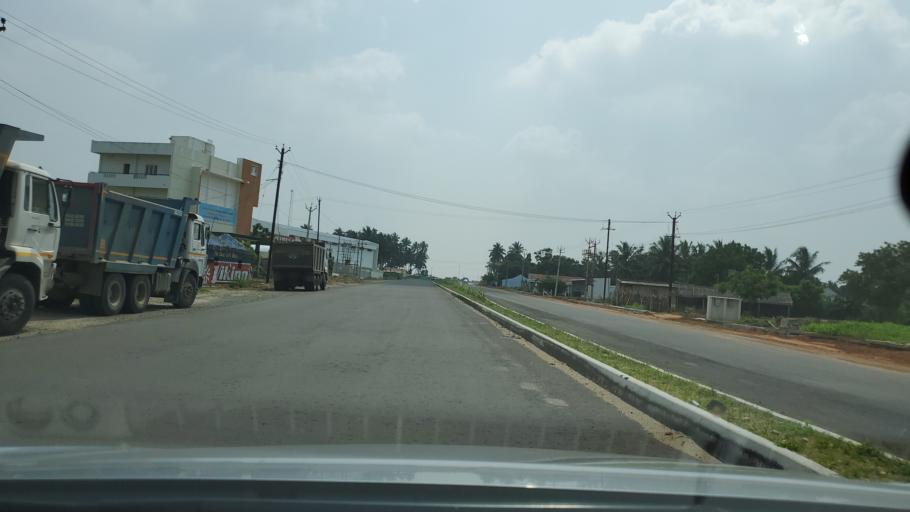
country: IN
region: Tamil Nadu
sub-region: Tiruppur
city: Kangayam
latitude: 10.9089
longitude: 77.4580
